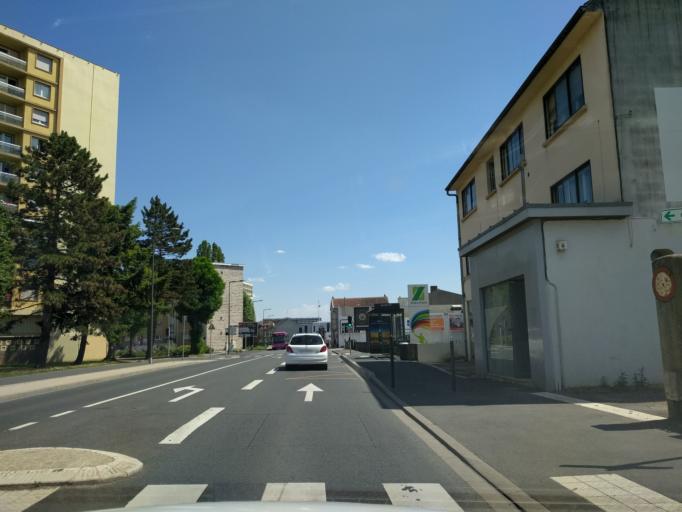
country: FR
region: Lorraine
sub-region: Departement de la Moselle
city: Le Ban Saint-Martin
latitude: 49.1348
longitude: 6.1610
